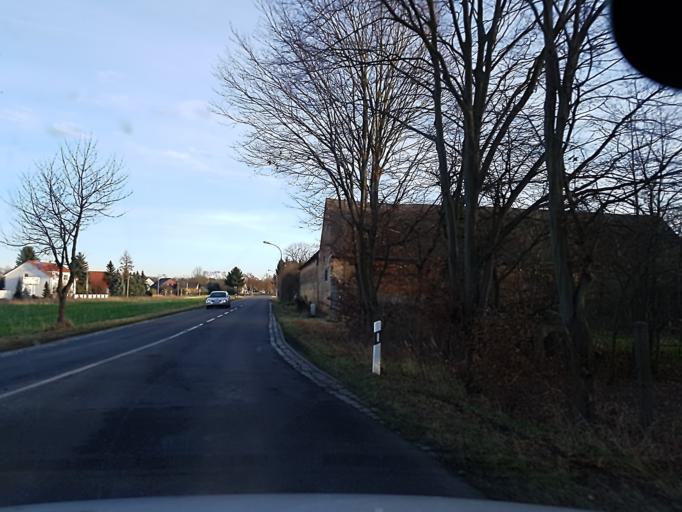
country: DE
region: Brandenburg
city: Finsterwalde
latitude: 51.6150
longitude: 13.7546
